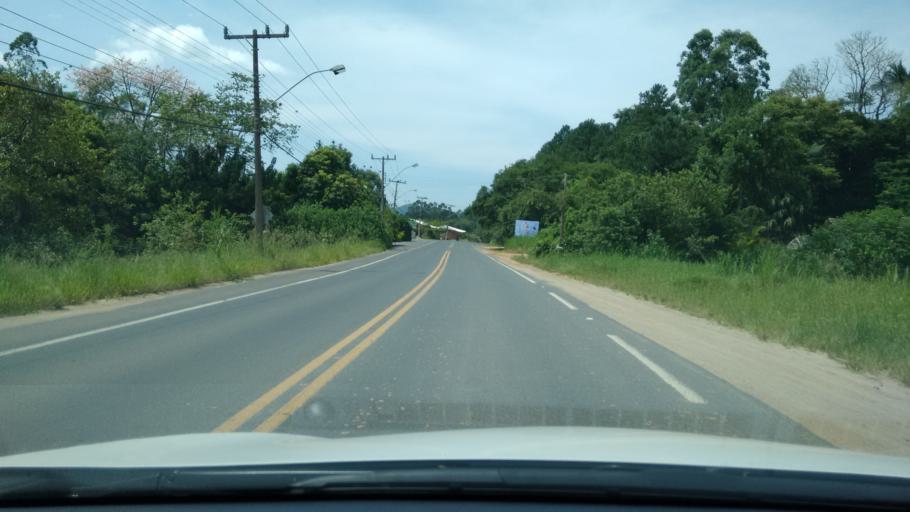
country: BR
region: Santa Catarina
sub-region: Timbo
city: Timbo
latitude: -26.8274
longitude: -49.2957
